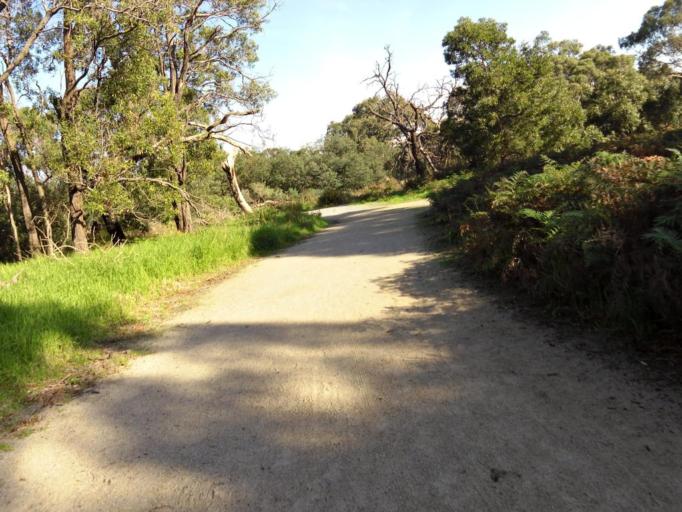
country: AU
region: Victoria
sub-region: Kingston
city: Dingley Village
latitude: -37.9951
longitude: 145.1307
